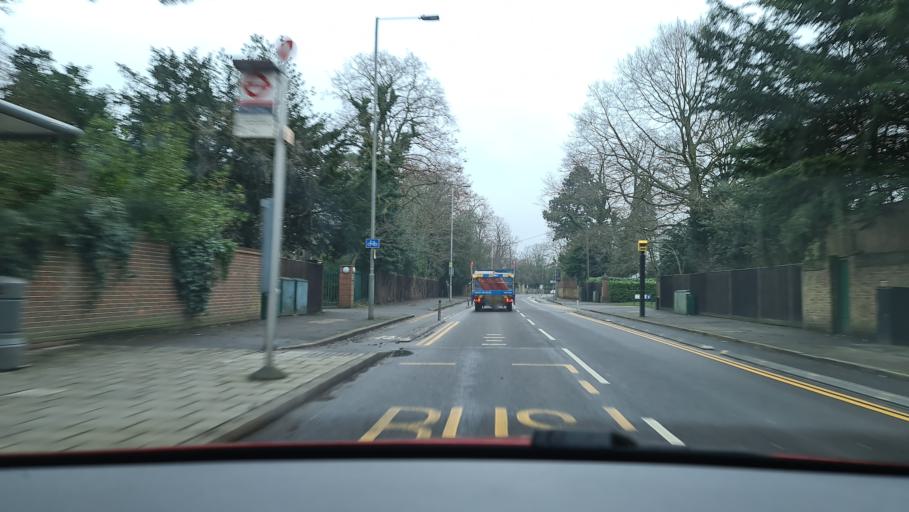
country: GB
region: England
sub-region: Greater London
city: Kingston upon Thames
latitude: 51.4253
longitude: -0.2744
